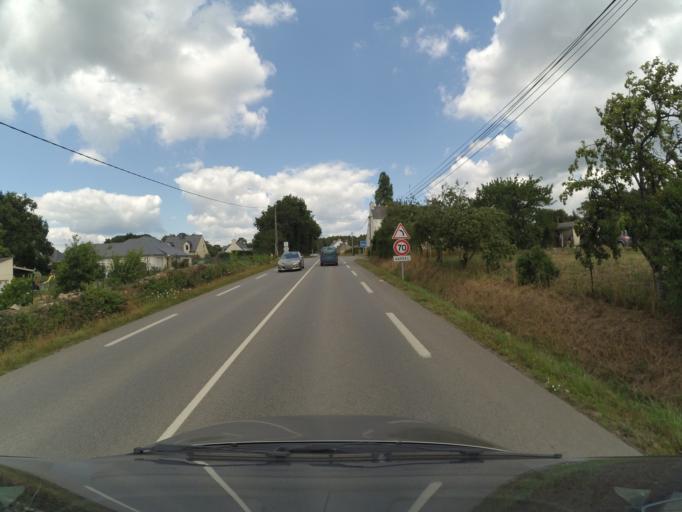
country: FR
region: Brittany
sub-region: Departement du Morbihan
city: Brech
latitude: 47.7055
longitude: -3.0071
